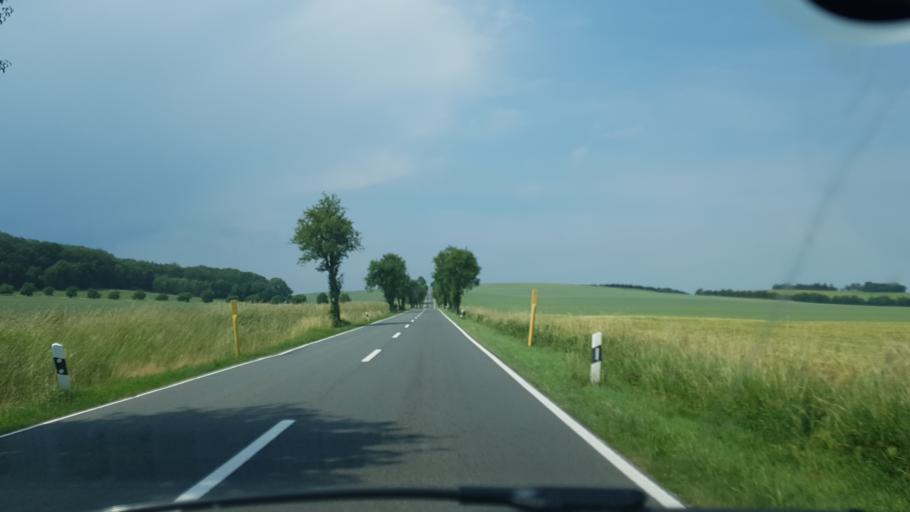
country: DE
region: Saxony-Anhalt
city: Osterwieck
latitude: 51.9686
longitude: 10.6943
